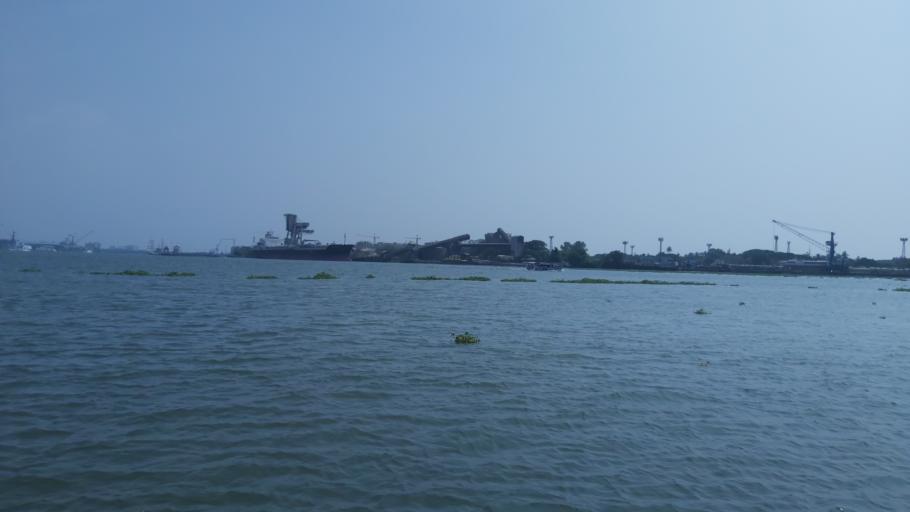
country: IN
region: Kerala
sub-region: Ernakulam
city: Cochin
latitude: 9.9707
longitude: 76.2720
